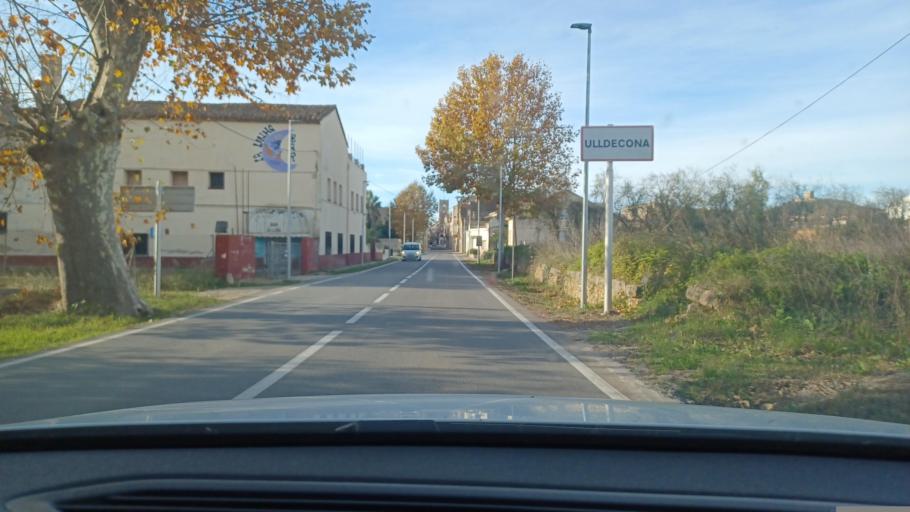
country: ES
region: Catalonia
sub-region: Provincia de Tarragona
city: Ulldecona
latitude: 40.6003
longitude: 0.4510
